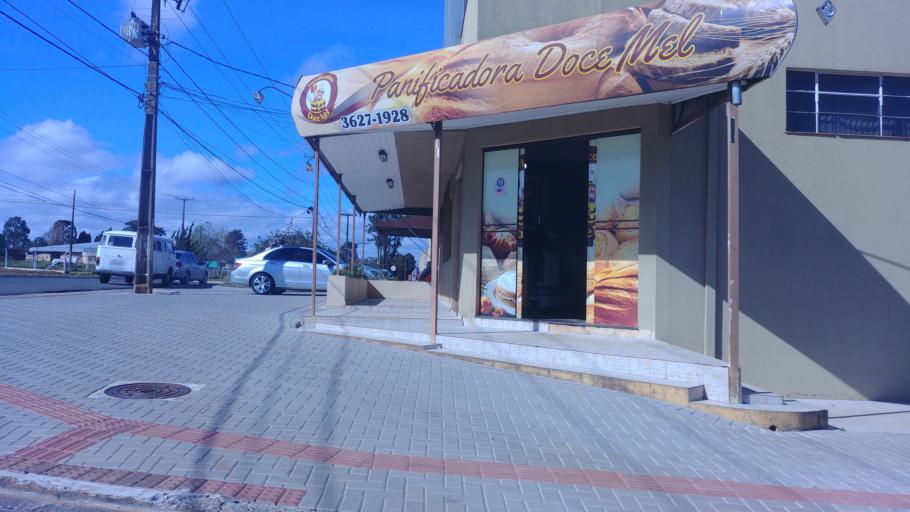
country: BR
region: Parana
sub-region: Guarapuava
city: Guarapuava
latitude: -25.3976
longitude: -51.4563
